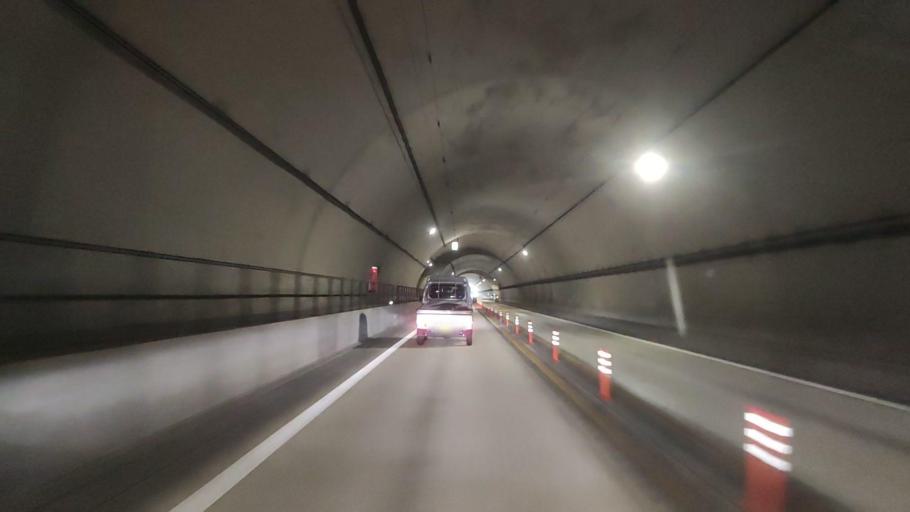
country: JP
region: Wakayama
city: Tanabe
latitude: 33.6093
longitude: 135.4268
